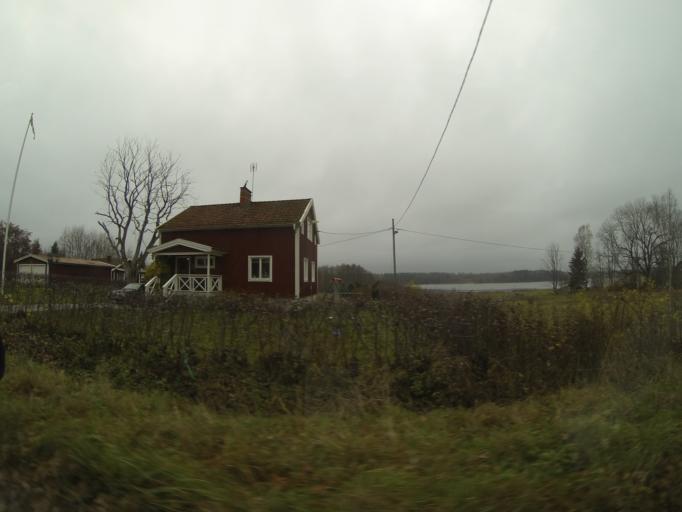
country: SE
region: Vaestmanland
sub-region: Surahammars Kommun
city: Surahammar
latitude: 59.6746
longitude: 16.0764
